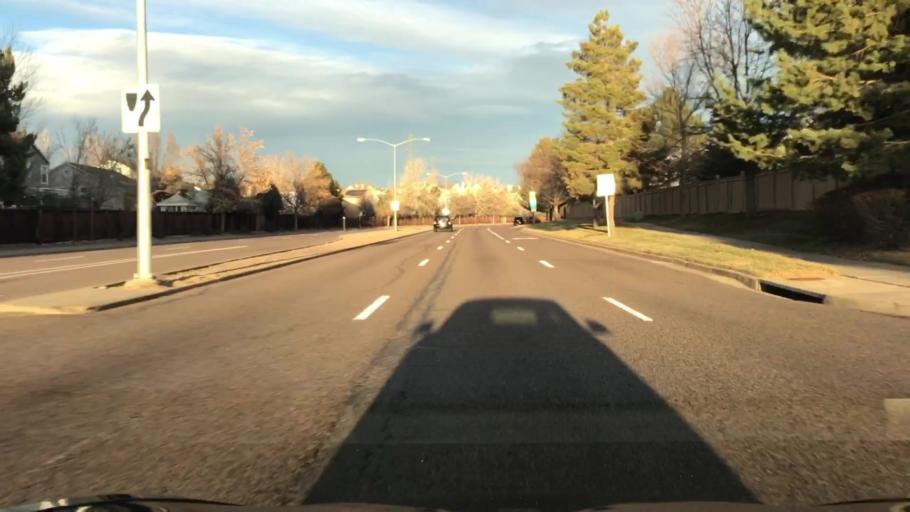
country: US
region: Colorado
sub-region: Adams County
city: Aurora
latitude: 39.6761
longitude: -104.7754
